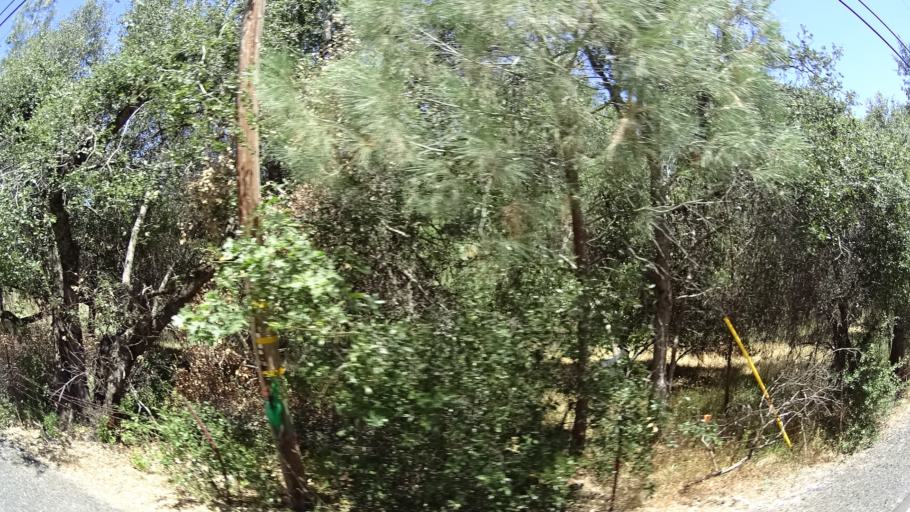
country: US
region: California
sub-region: Calaveras County
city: Mountain Ranch
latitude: 38.2473
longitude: -120.5183
